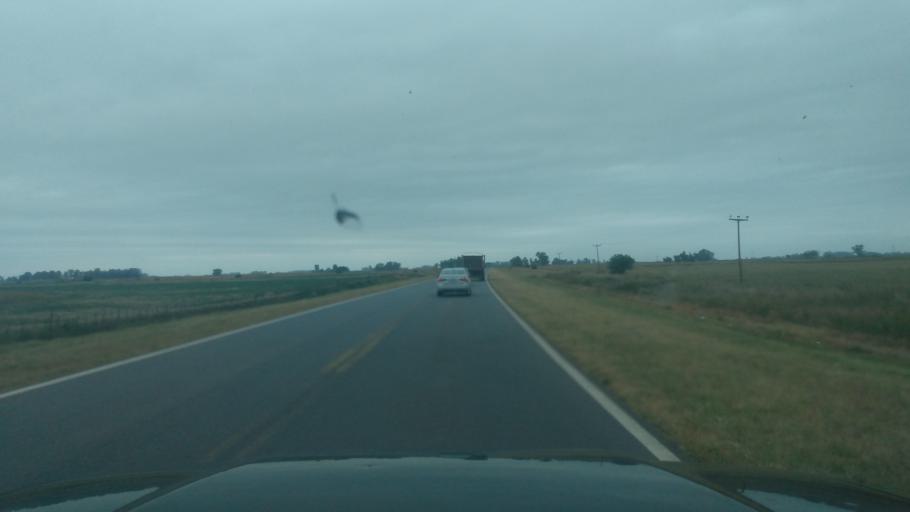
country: AR
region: Buenos Aires
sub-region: Partido de Nueve de Julio
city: Nueve de Julio
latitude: -35.3995
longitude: -60.7613
